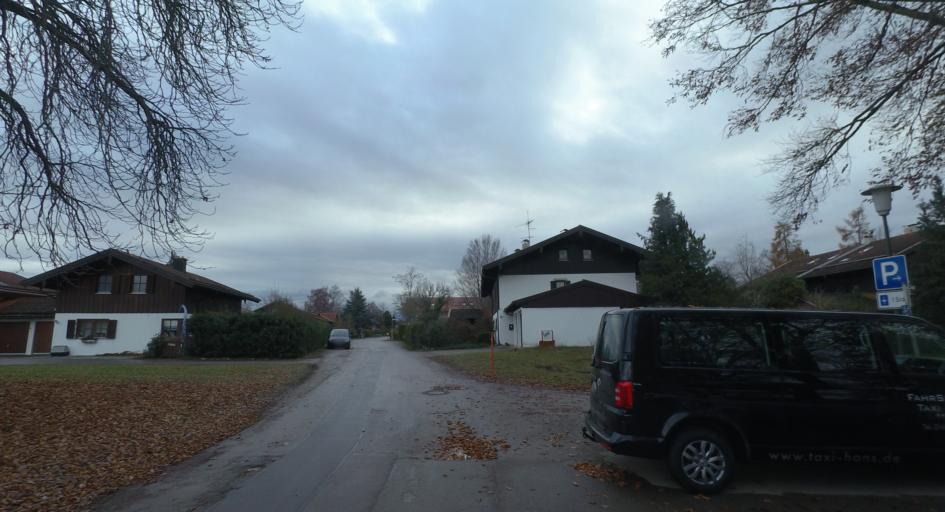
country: DE
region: Bavaria
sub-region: Upper Bavaria
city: Chieming
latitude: 47.8969
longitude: 12.5400
